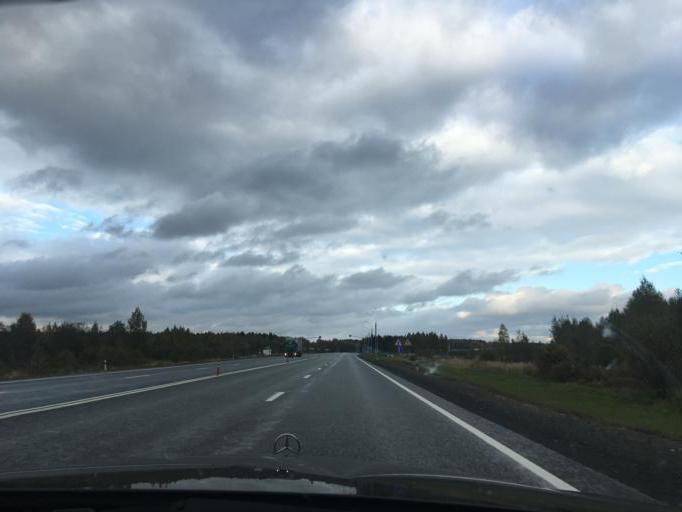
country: RU
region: Smolensk
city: Golynki
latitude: 54.7184
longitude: 31.2743
